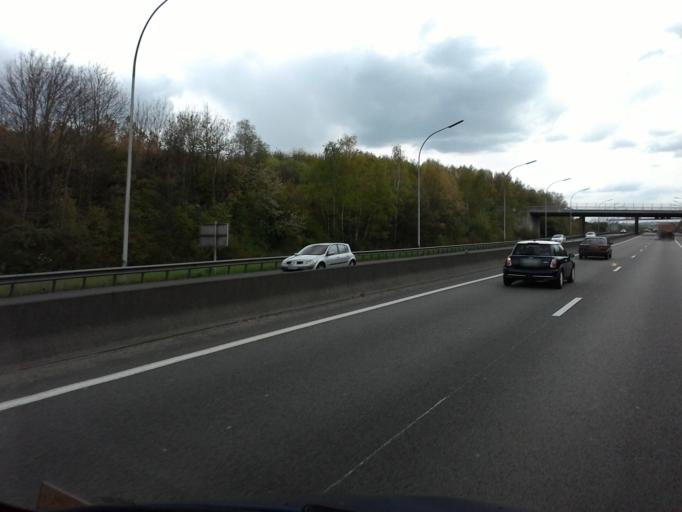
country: LU
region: Luxembourg
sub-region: Canton de Luxembourg
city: Strassen
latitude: 49.6143
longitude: 6.0826
